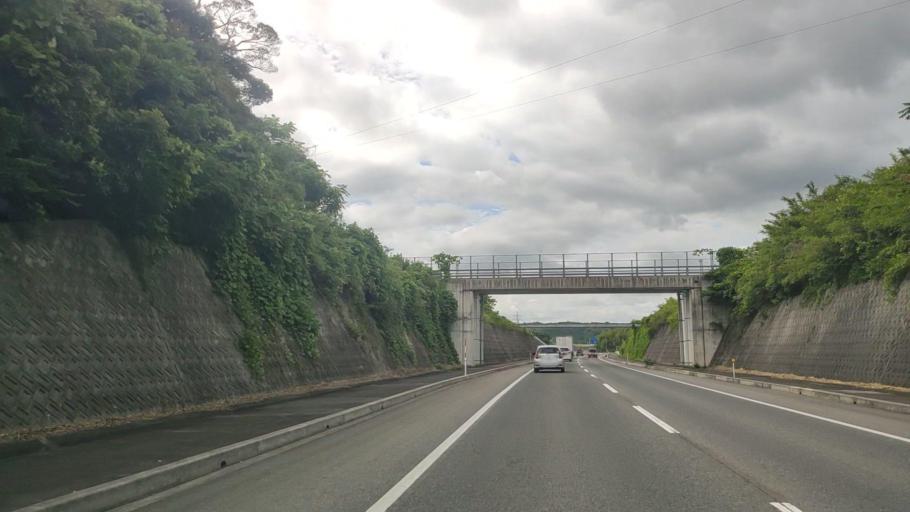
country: JP
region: Tottori
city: Yonago
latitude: 35.3919
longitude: 133.3826
